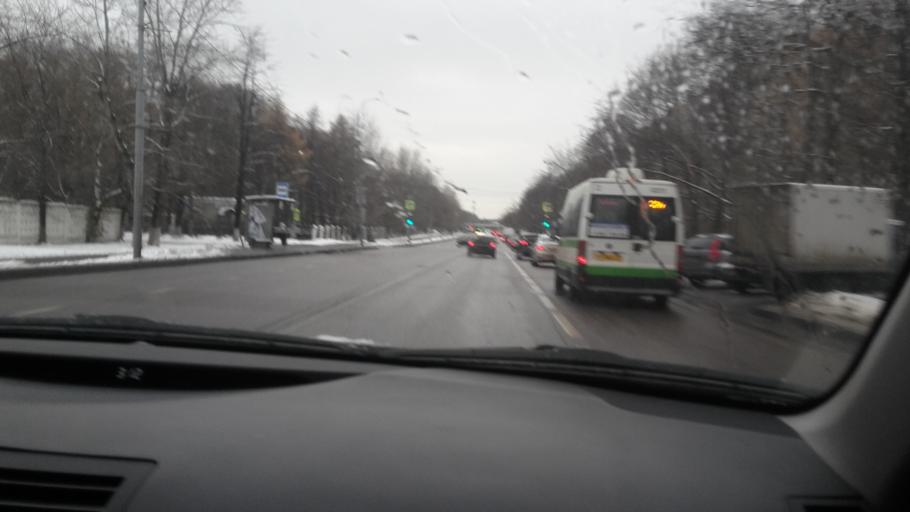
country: RU
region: Moscow
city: Kuz'minki
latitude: 55.7064
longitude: 37.7942
